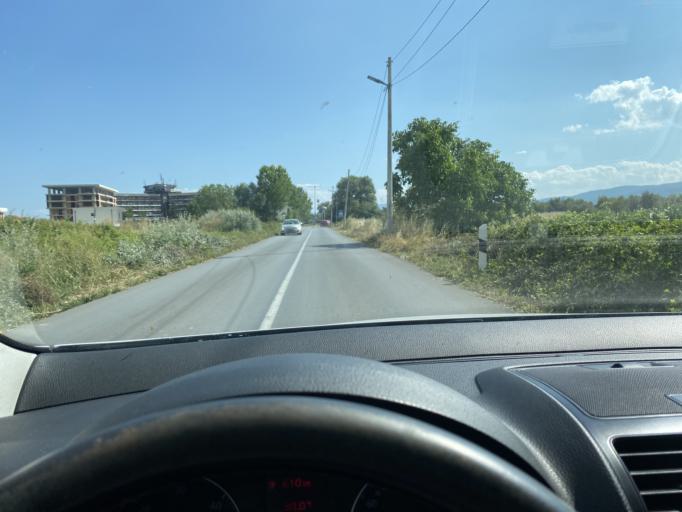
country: MK
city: Misleshevo
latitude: 41.1750
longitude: 20.7064
